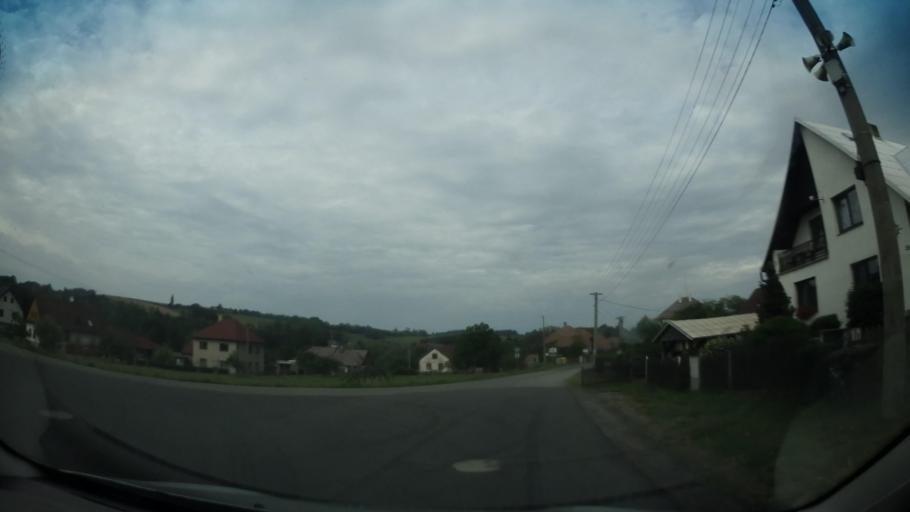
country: CZ
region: Pardubicky
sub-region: Okres Chrudim
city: Sec
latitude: 49.8376
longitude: 15.6983
